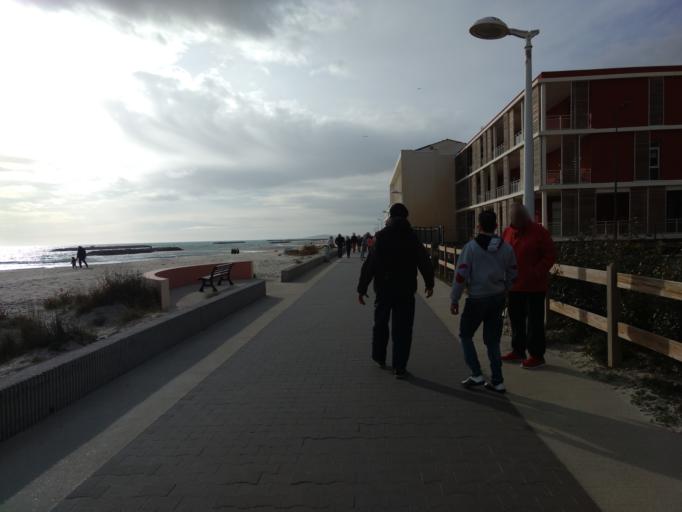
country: FR
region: Languedoc-Roussillon
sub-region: Departement de l'Herault
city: Palavas-les-Flots
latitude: 43.5243
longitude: 3.9249
